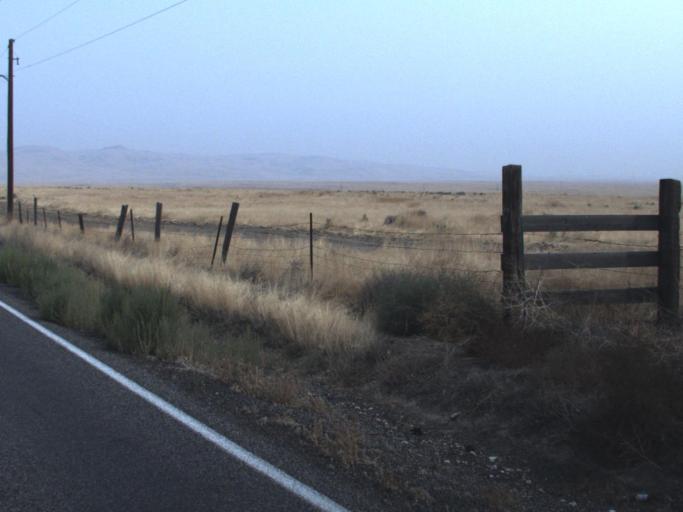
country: US
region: Washington
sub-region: Yakima County
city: Sunnyside
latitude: 46.3934
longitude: -119.9538
